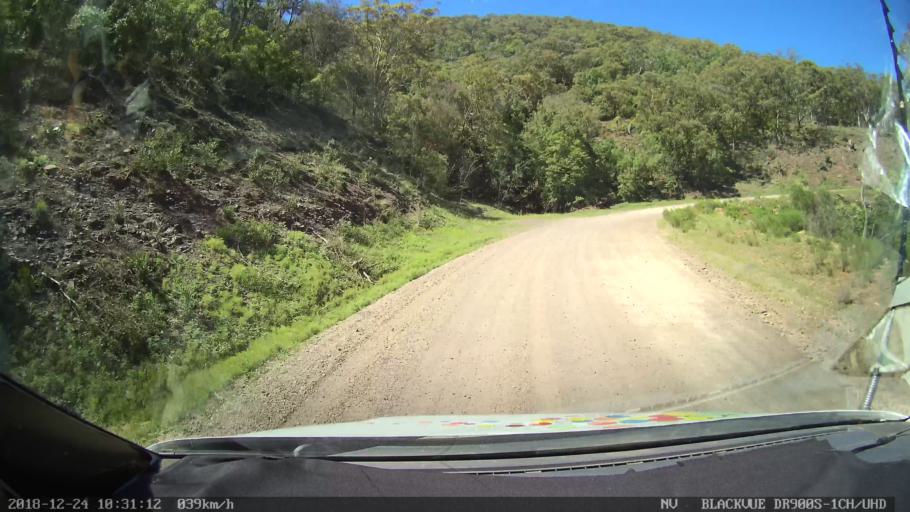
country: AU
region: New South Wales
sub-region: Upper Hunter Shire
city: Merriwa
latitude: -31.8387
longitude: 150.5229
